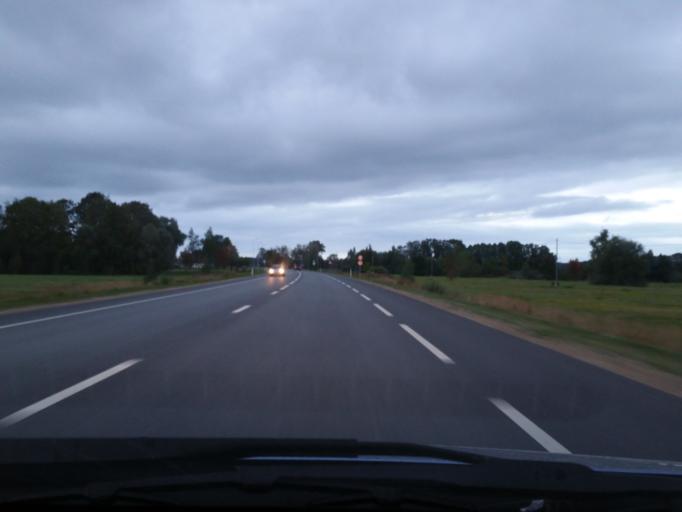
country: LV
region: Adazi
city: Adazi
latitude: 57.1041
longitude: 24.3139
